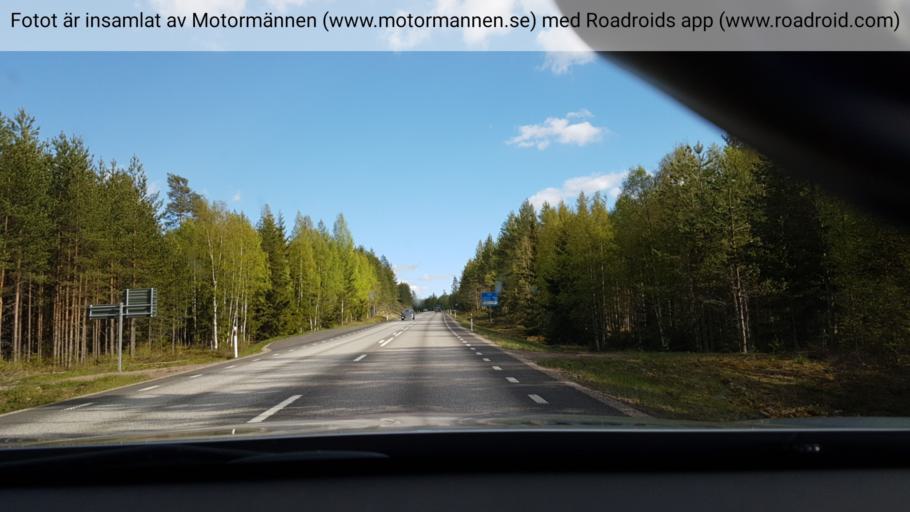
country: SE
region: Dalarna
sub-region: Faluns Kommun
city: Bjursas
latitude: 60.7922
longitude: 15.2778
